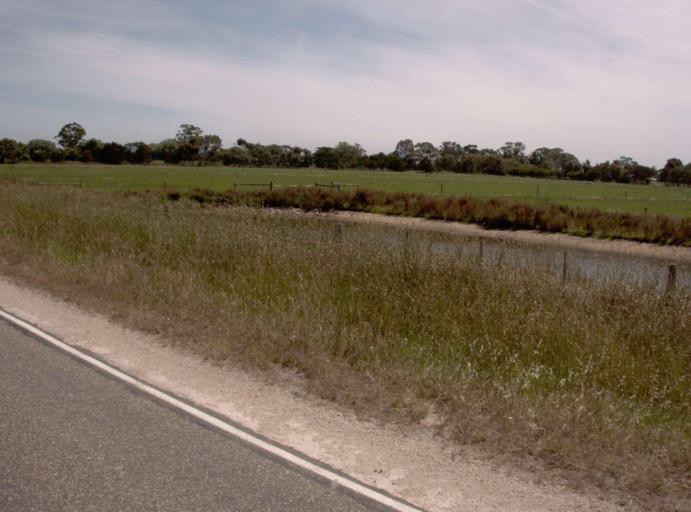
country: AU
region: Victoria
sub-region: Wellington
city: Heyfield
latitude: -38.0511
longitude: 146.8749
